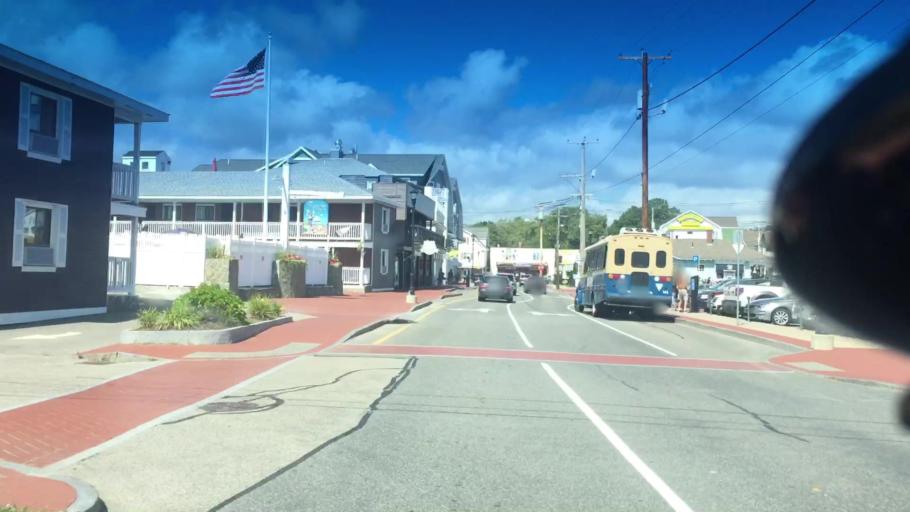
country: US
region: Maine
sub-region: York County
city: York Beach
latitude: 43.1744
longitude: -70.6095
